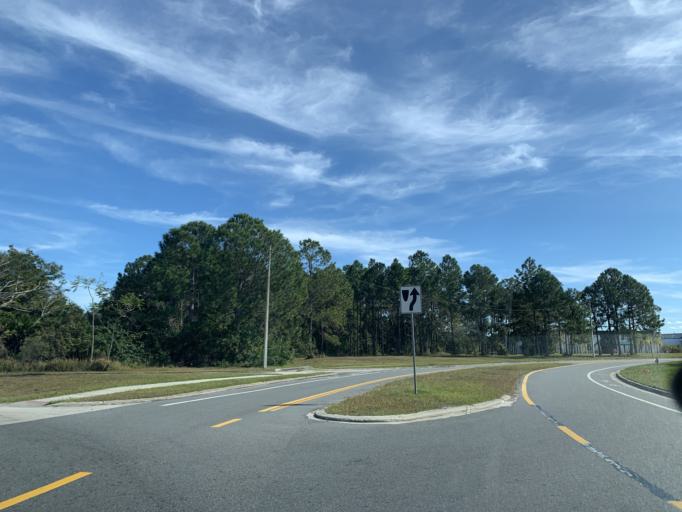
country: US
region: Florida
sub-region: Orange County
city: Tangelo Park
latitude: 28.4559
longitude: -81.4615
